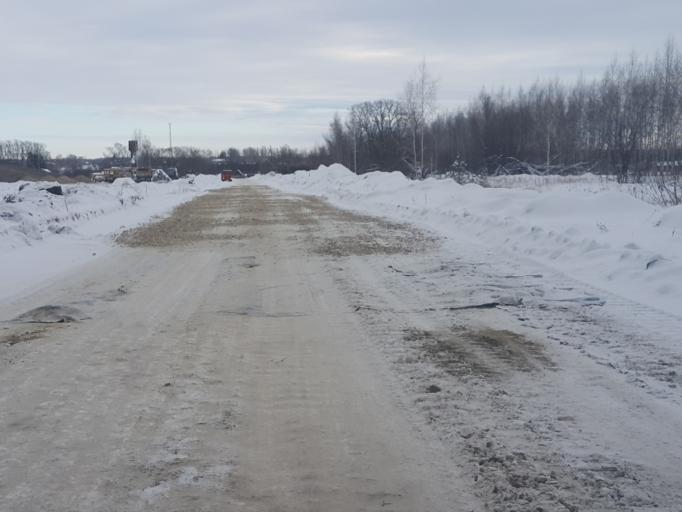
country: RU
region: Tambov
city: Platonovka
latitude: 52.8818
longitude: 41.8701
